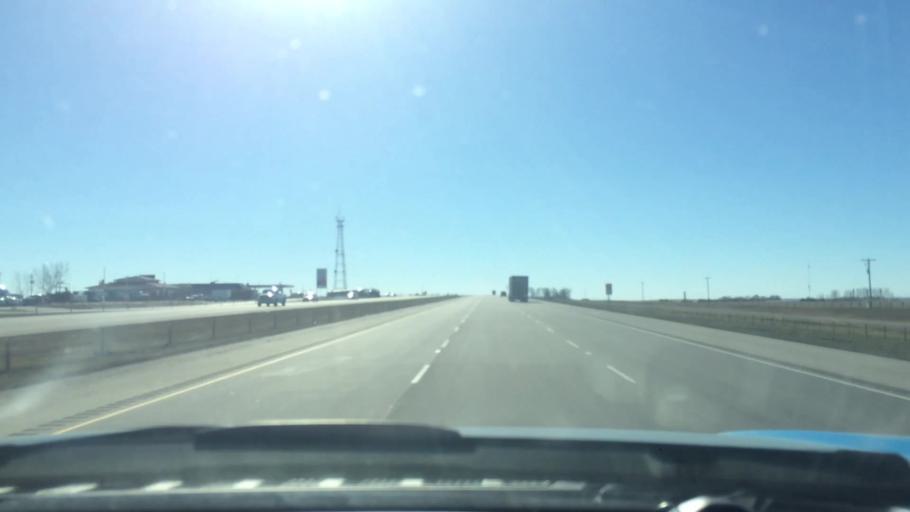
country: CA
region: Alberta
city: Crossfield
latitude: 51.4153
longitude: -114.0020
